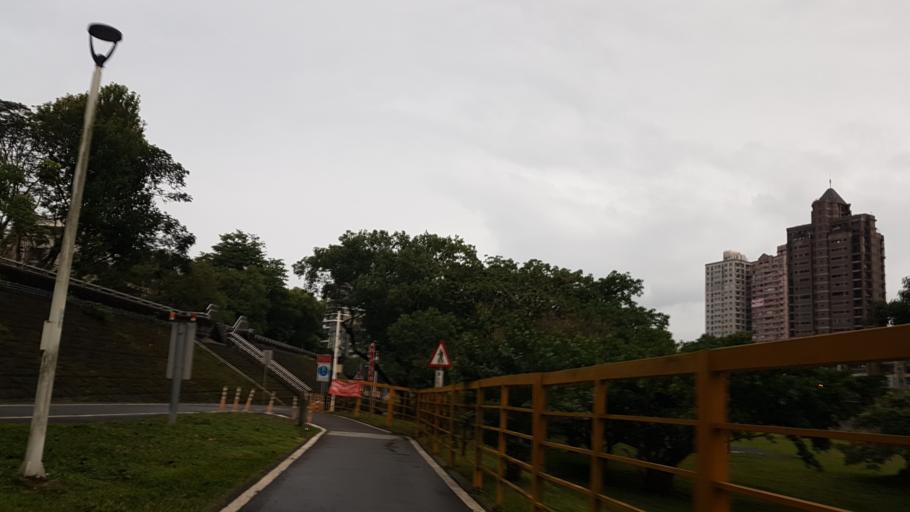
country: TW
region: Taipei
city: Taipei
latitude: 24.9858
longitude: 121.5450
